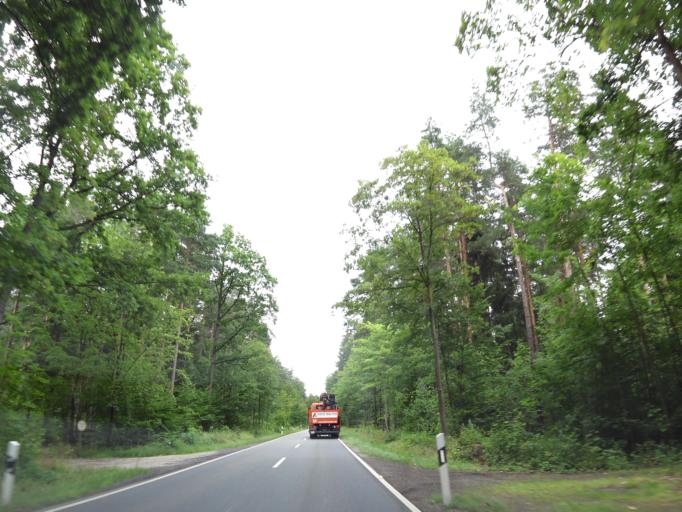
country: DE
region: Thuringia
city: Hainspitz
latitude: 50.9433
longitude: 11.8550
